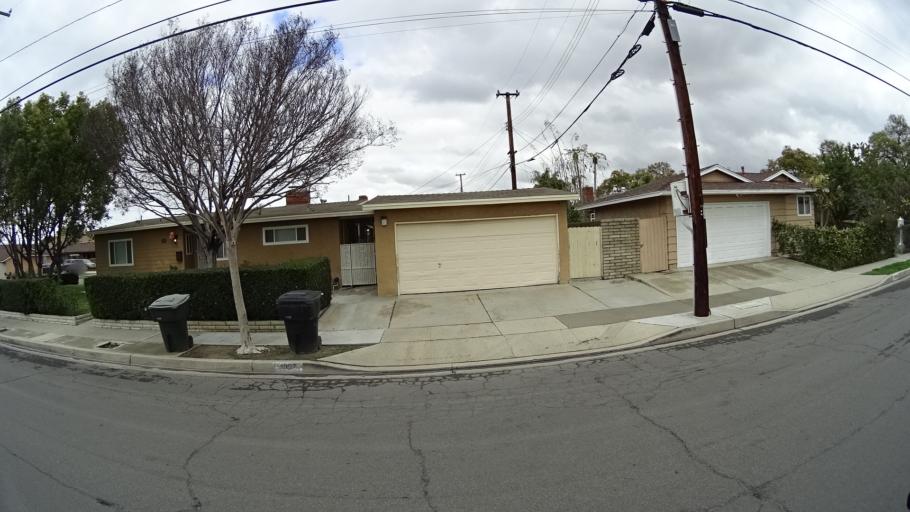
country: US
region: California
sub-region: Orange County
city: Anaheim
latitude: 33.8296
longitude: -117.9507
